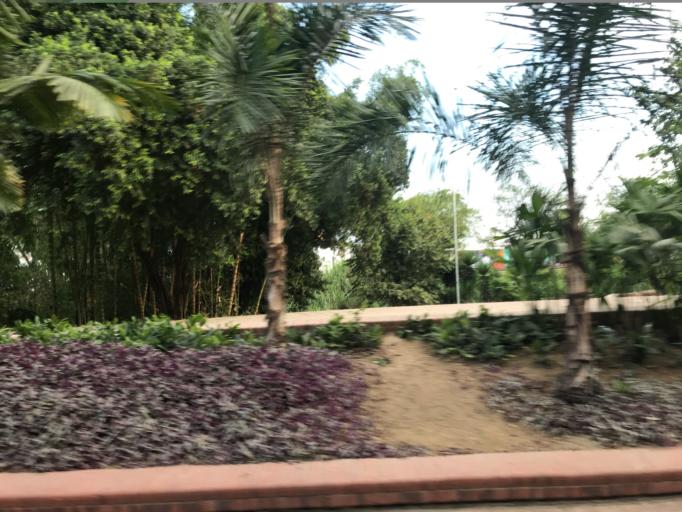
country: CO
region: Valle del Cauca
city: Cali
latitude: 3.4609
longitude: -76.5262
